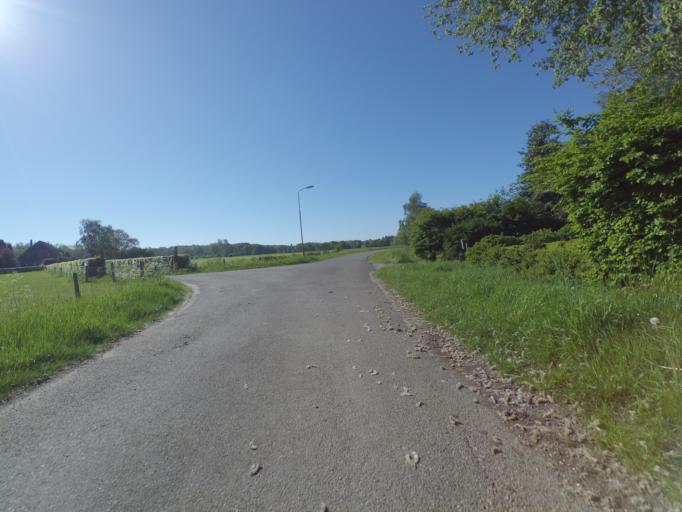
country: NL
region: Gelderland
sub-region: Gemeente Voorst
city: Voorst
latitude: 52.1338
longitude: 6.1293
